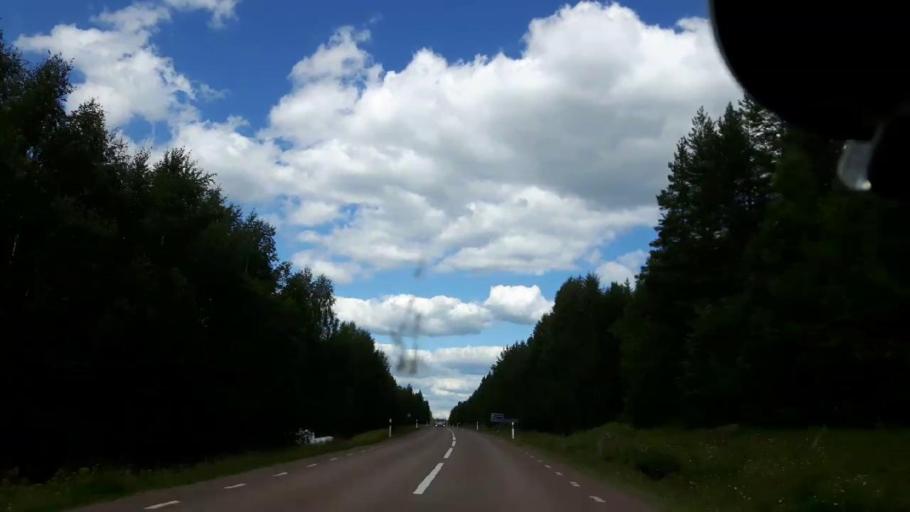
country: SE
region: Jaemtland
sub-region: Ragunda Kommun
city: Hammarstrand
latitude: 62.9230
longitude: 16.7027
